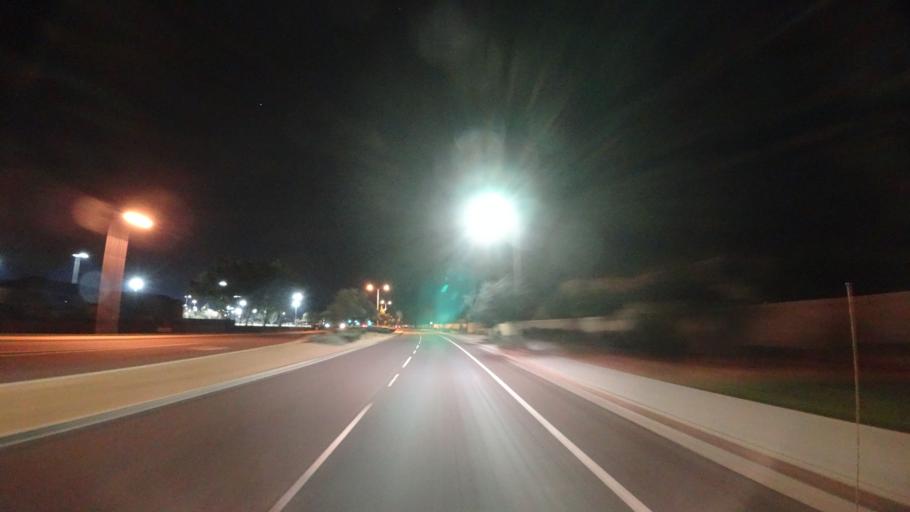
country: US
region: Arizona
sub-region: Maricopa County
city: Sun Lakes
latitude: 33.2433
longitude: -111.8660
